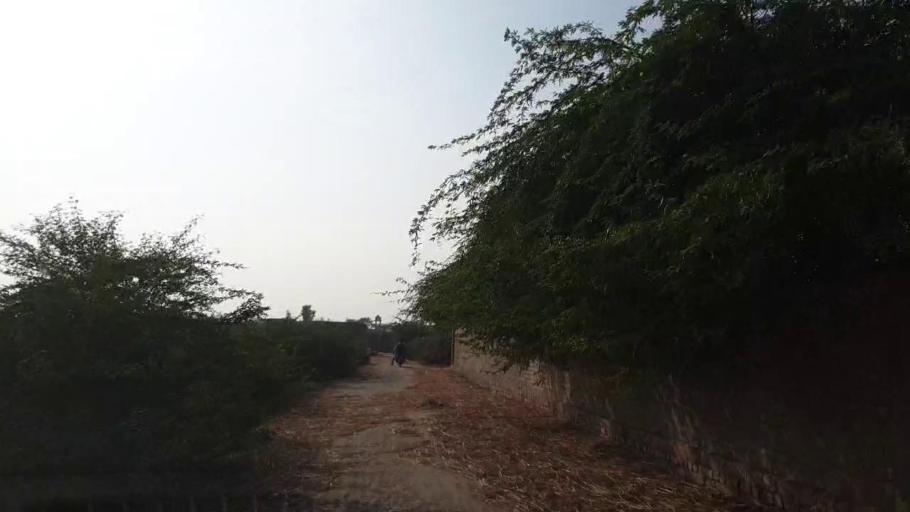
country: PK
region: Sindh
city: Kario
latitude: 24.9264
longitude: 68.5642
